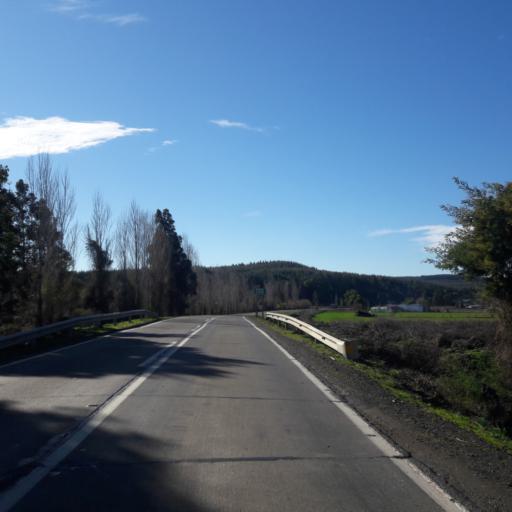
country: CL
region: Araucania
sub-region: Provincia de Malleco
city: Collipulli
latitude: -37.7833
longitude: -72.5201
